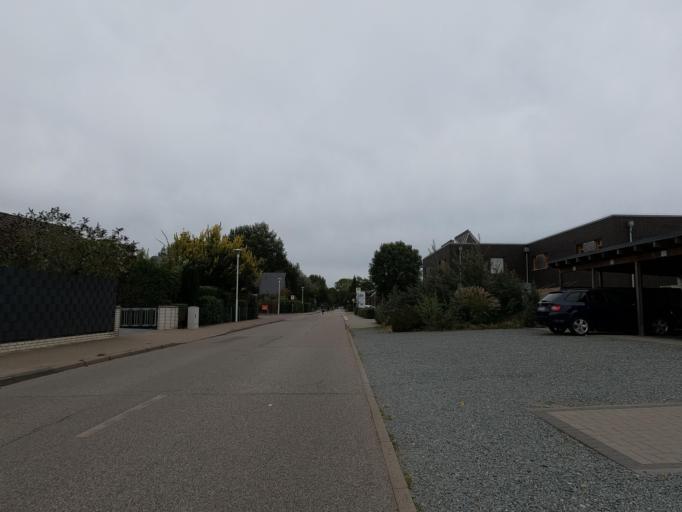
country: DE
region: Schleswig-Holstein
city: Gromitz
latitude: 54.1532
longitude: 10.9717
